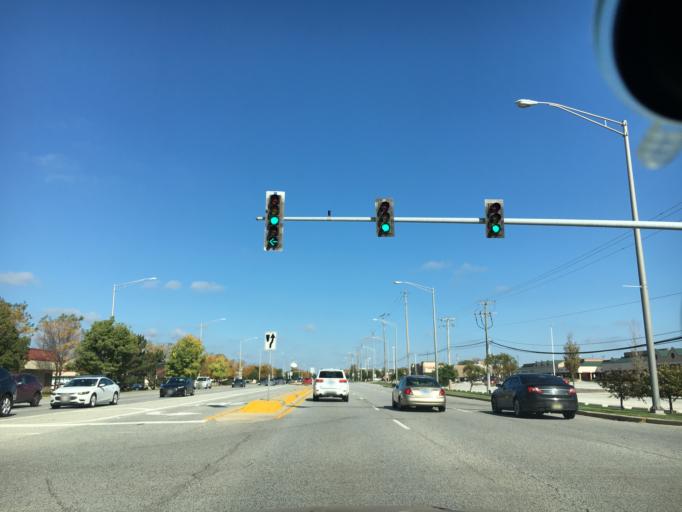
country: US
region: Illinois
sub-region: Cook County
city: Tinley Park
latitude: 41.5985
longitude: -87.7939
